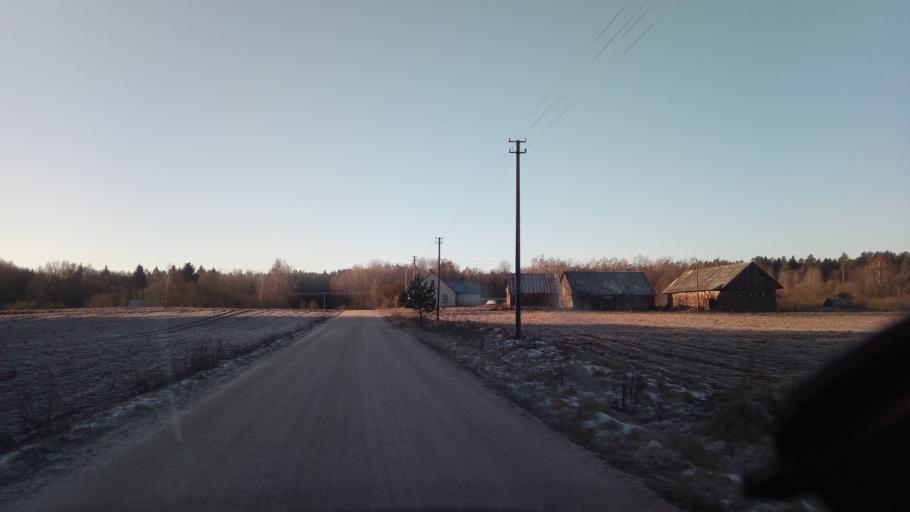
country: LT
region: Alytaus apskritis
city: Druskininkai
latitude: 54.1595
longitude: 23.9545
